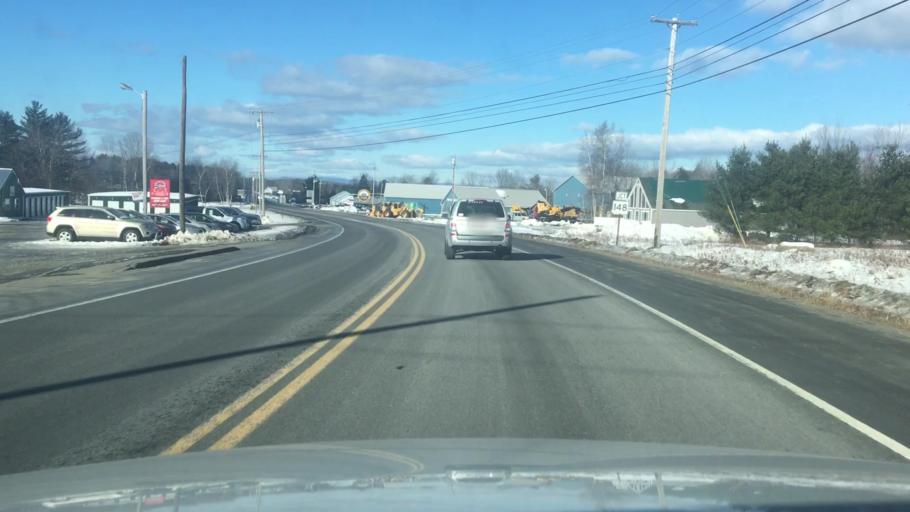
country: US
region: Maine
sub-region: Somerset County
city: Skowhegan
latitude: 44.8131
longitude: -69.7609
